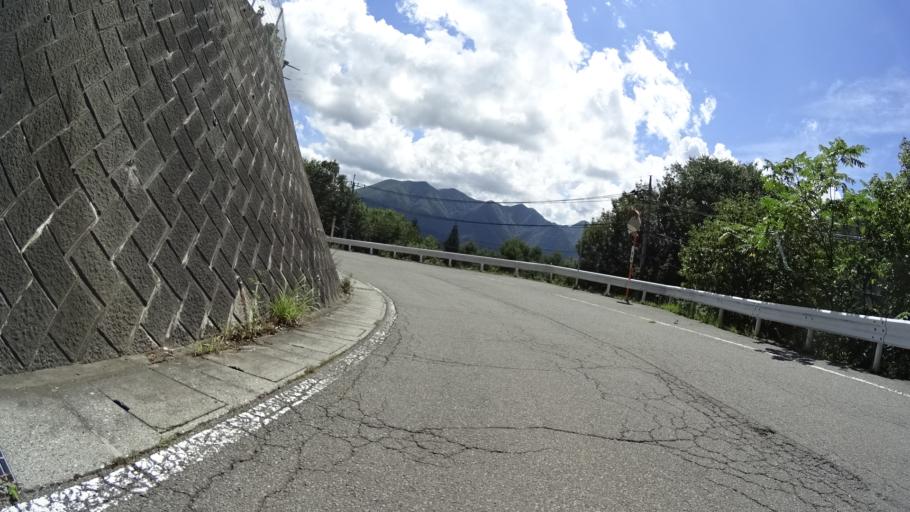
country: JP
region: Yamanashi
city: Enzan
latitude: 35.6588
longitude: 138.8120
